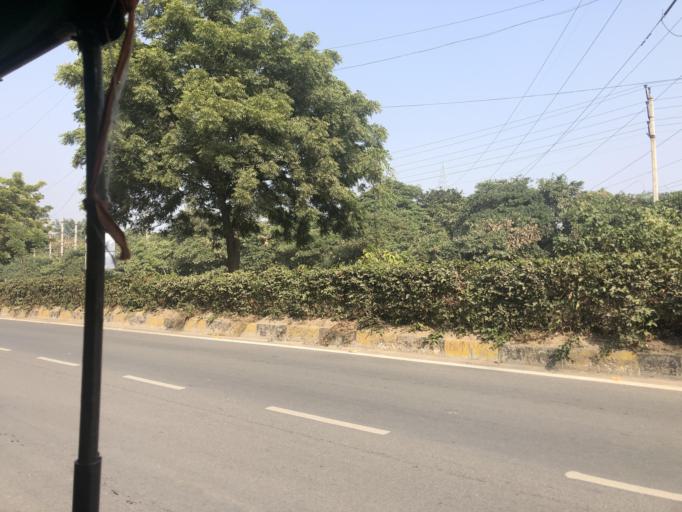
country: IN
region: Haryana
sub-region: Gurgaon
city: Gurgaon
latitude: 28.4445
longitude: 77.0826
